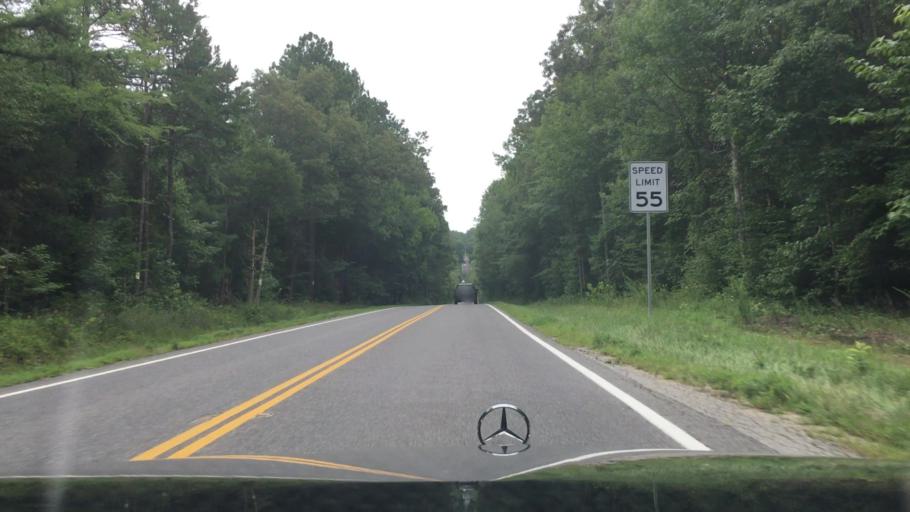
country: US
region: Virginia
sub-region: Nottoway County
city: Crewe
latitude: 37.2767
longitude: -78.1798
